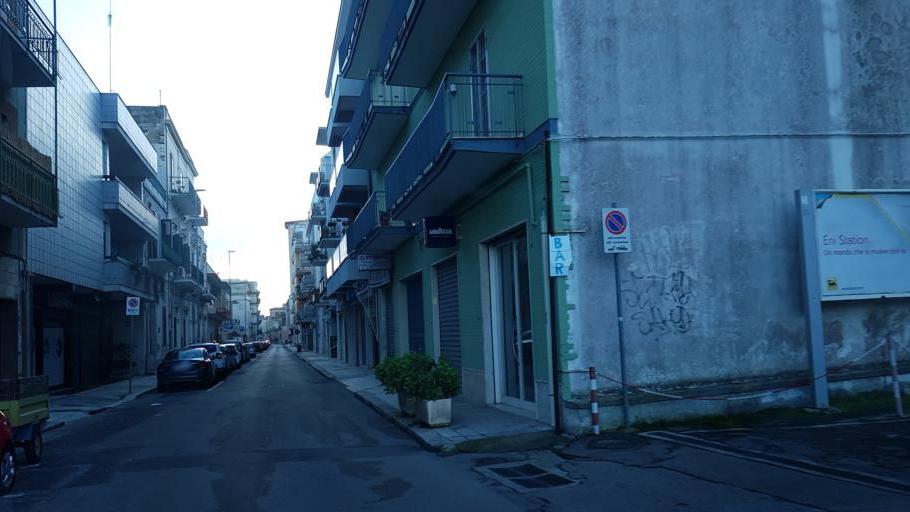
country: IT
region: Apulia
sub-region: Provincia di Lecce
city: Lecce
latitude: 40.3622
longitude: 18.1765
